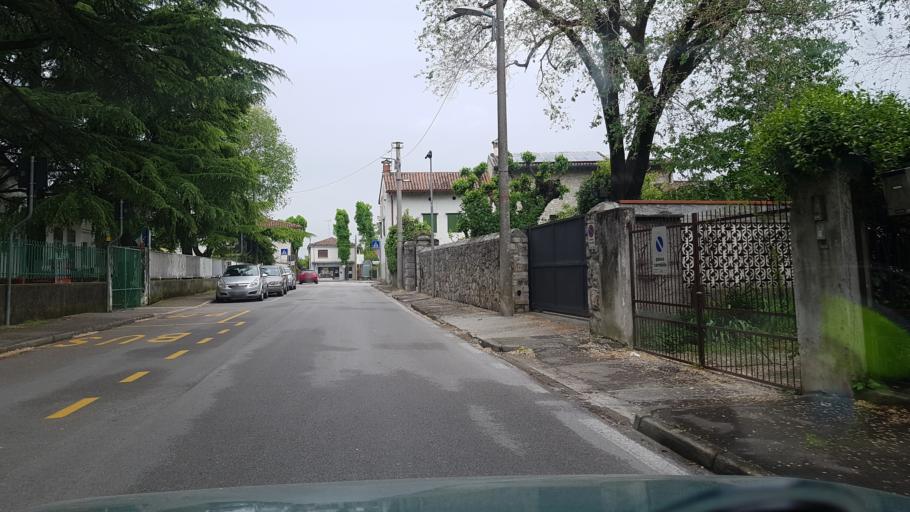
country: IT
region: Friuli Venezia Giulia
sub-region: Provincia di Gorizia
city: Ronchi dei Legionari
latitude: 45.8341
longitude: 13.5114
